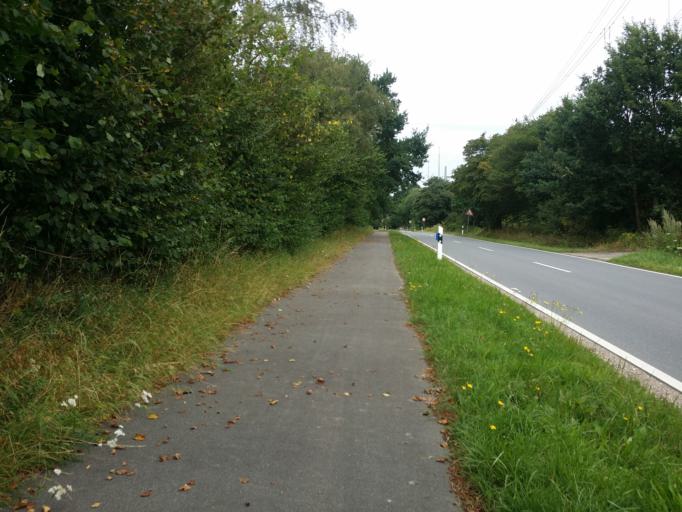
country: DE
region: Schleswig-Holstein
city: Oldendorf
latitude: 53.9655
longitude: 9.4479
